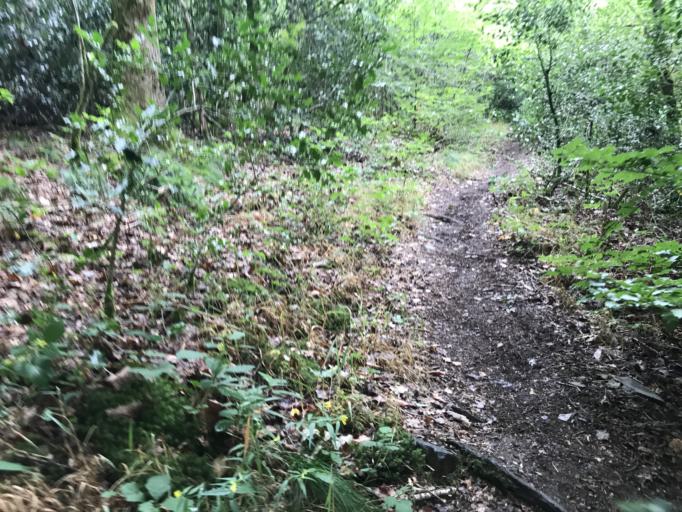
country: FR
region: Champagne-Ardenne
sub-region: Departement des Ardennes
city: Montherme
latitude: 49.8921
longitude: 4.7511
